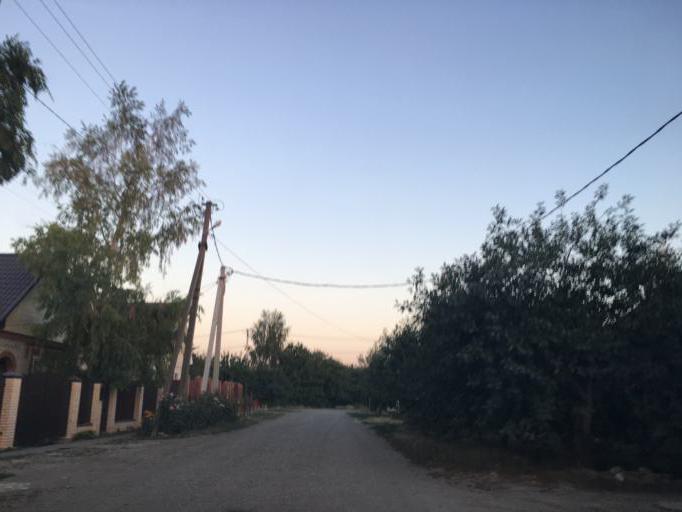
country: RU
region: Krasnodarskiy
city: Kushchevskaya
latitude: 46.5607
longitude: 39.6435
